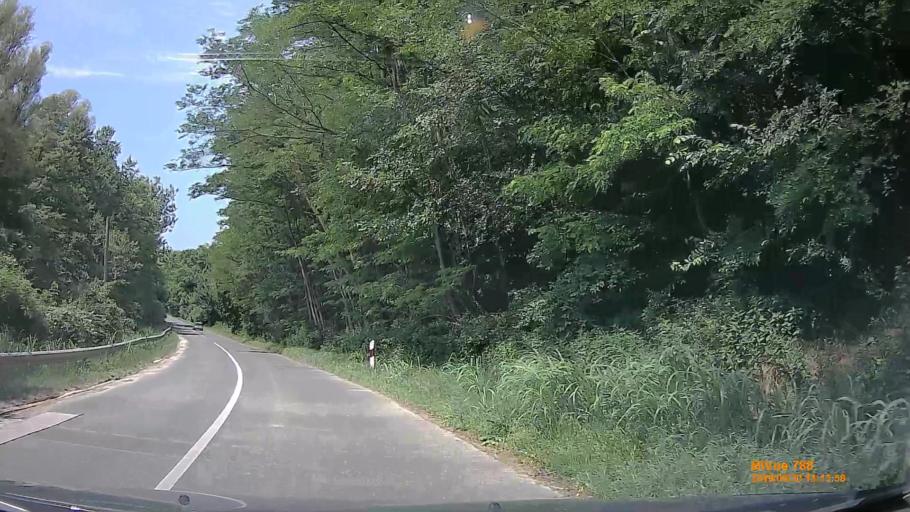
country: HU
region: Baranya
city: Pecsvarad
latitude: 46.1475
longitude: 18.5013
